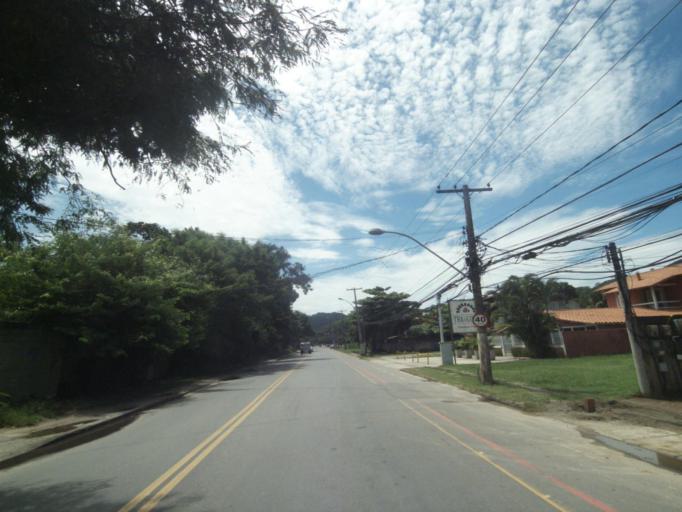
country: BR
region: Rio de Janeiro
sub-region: Niteroi
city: Niteroi
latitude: -22.9387
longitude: -43.0146
